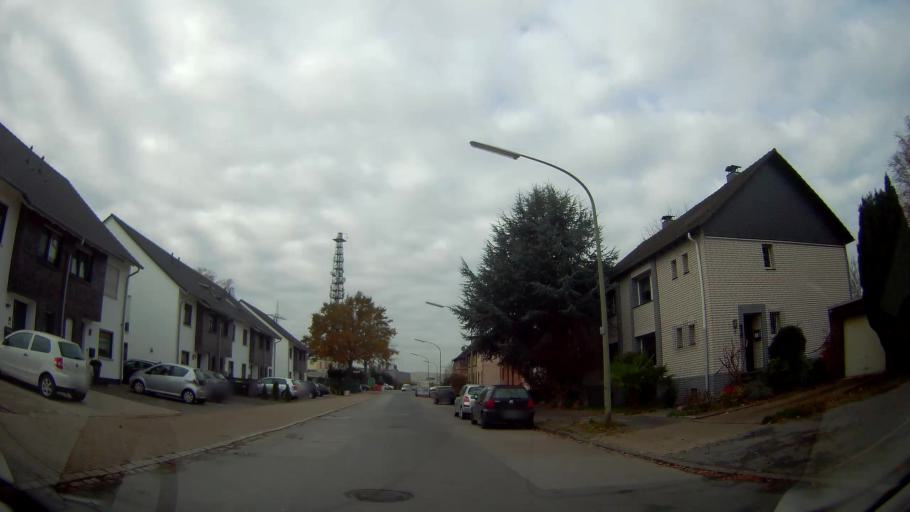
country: DE
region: North Rhine-Westphalia
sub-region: Regierungsbezirk Munster
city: Gelsenkirchen
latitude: 51.5287
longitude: 7.0979
